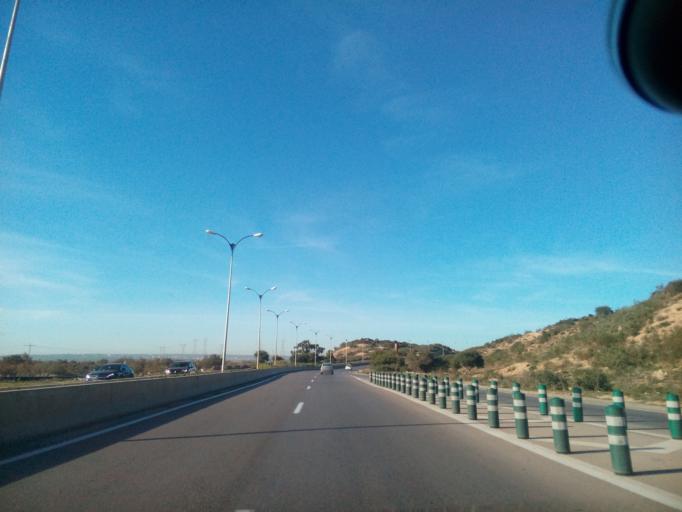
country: DZ
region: Oran
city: Ain el Bya
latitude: 35.7871
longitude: -0.1062
